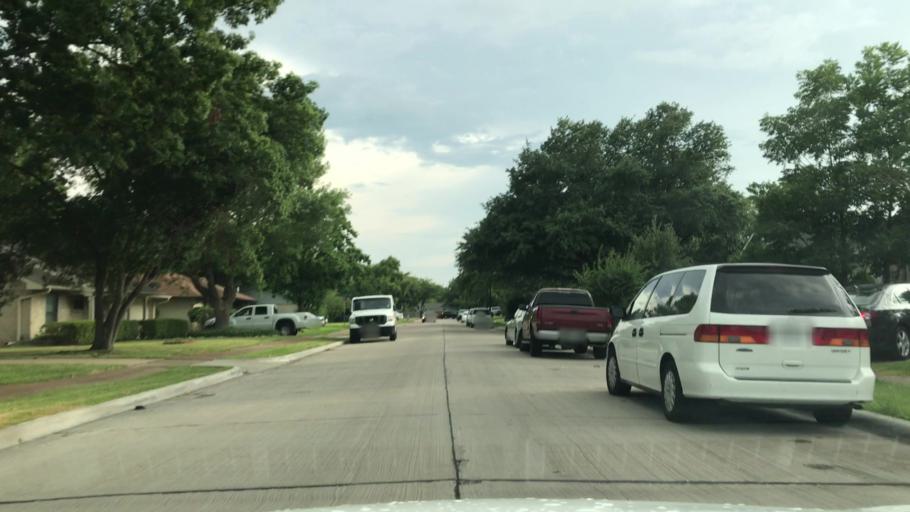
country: US
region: Texas
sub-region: Dallas County
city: Garland
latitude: 32.8595
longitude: -96.6368
